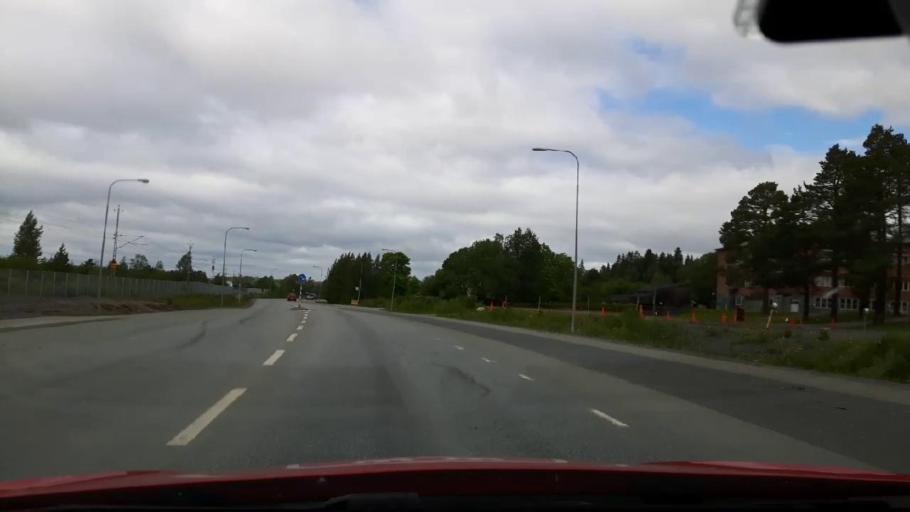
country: SE
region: Jaemtland
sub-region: Krokoms Kommun
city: Krokom
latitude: 63.3185
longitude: 14.4606
